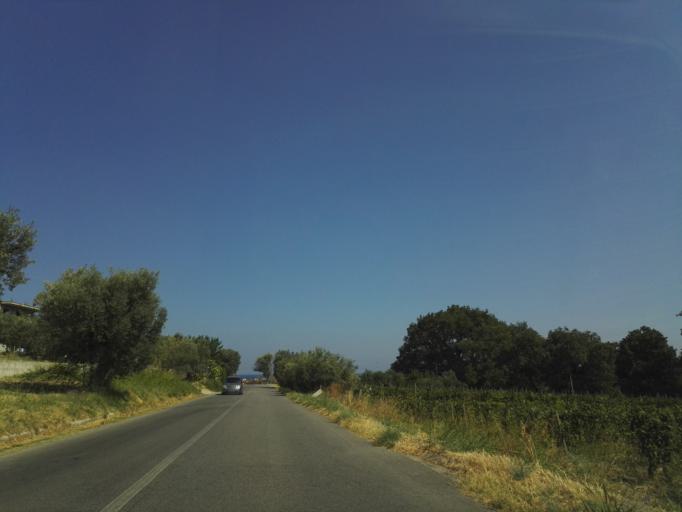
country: IT
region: Calabria
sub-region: Provincia di Reggio Calabria
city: Monasterace
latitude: 38.4406
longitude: 16.5443
